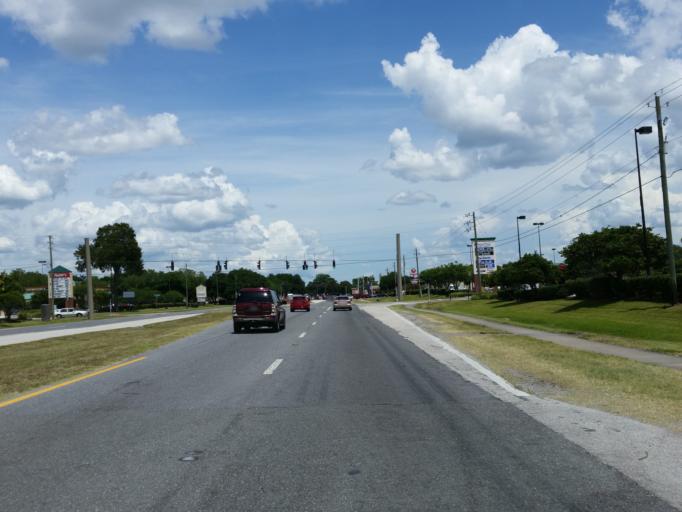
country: US
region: Florida
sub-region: Hillsborough County
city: Plant City
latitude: 27.9890
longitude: -82.1253
